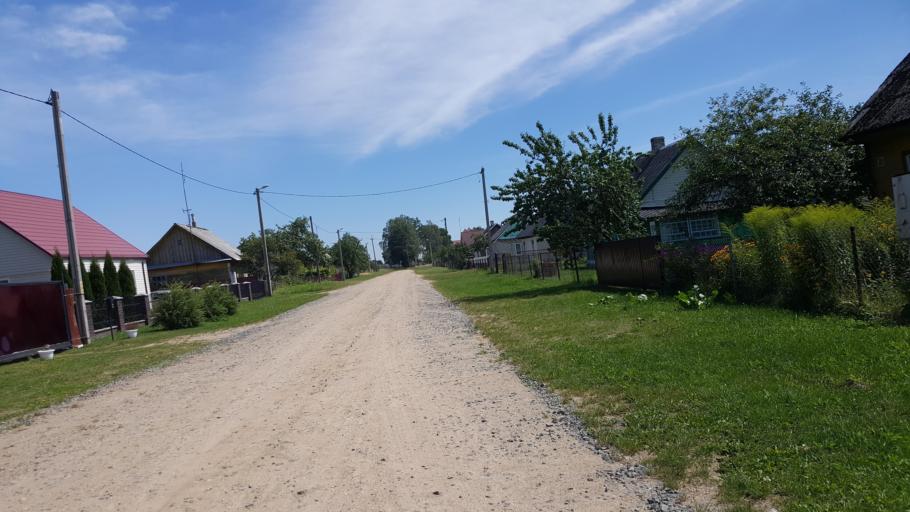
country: BY
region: Brest
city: Pruzhany
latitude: 52.5647
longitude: 24.2086
